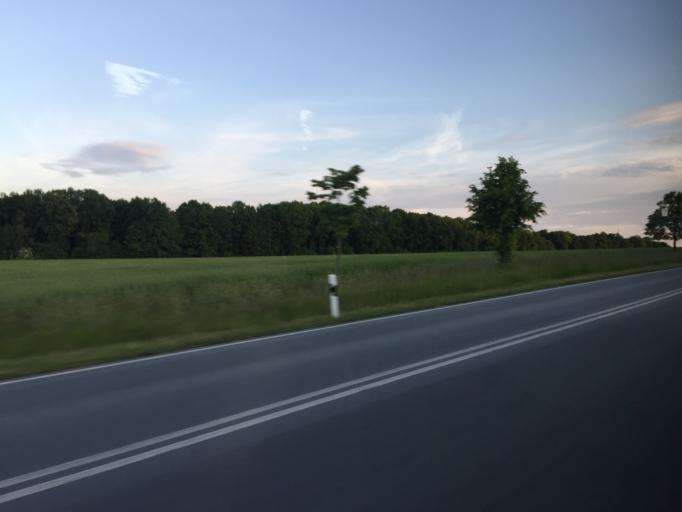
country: DE
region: Saxony
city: Sohland am Rotstein
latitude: 51.1230
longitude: 14.7422
